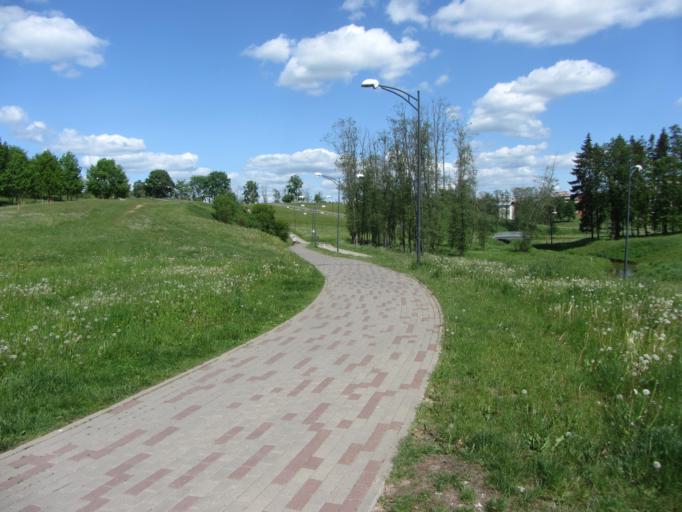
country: LT
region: Utenos apskritis
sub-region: Utena
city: Utena
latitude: 55.5059
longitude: 25.5890
